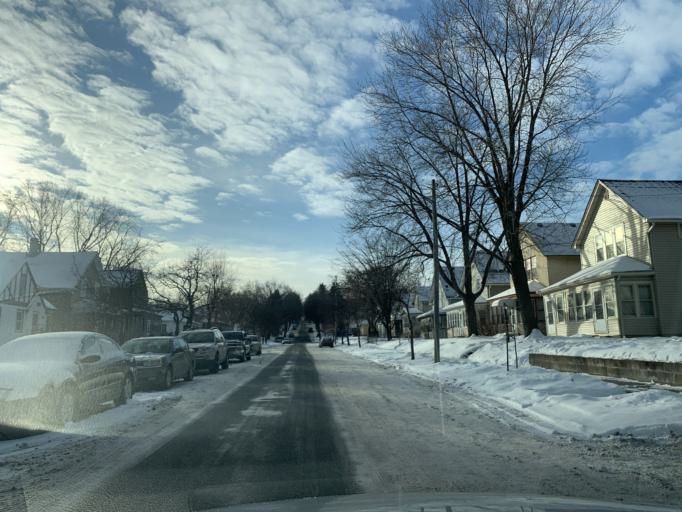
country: US
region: Minnesota
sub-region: Anoka County
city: Columbia Heights
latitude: 45.0253
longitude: -93.2866
